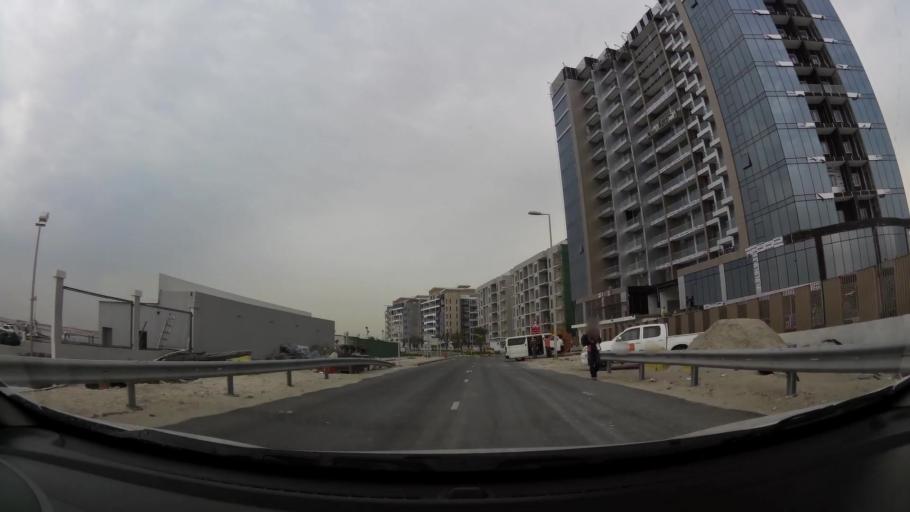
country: BH
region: Central Governorate
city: Dar Kulayb
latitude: 25.8680
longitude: 50.6106
